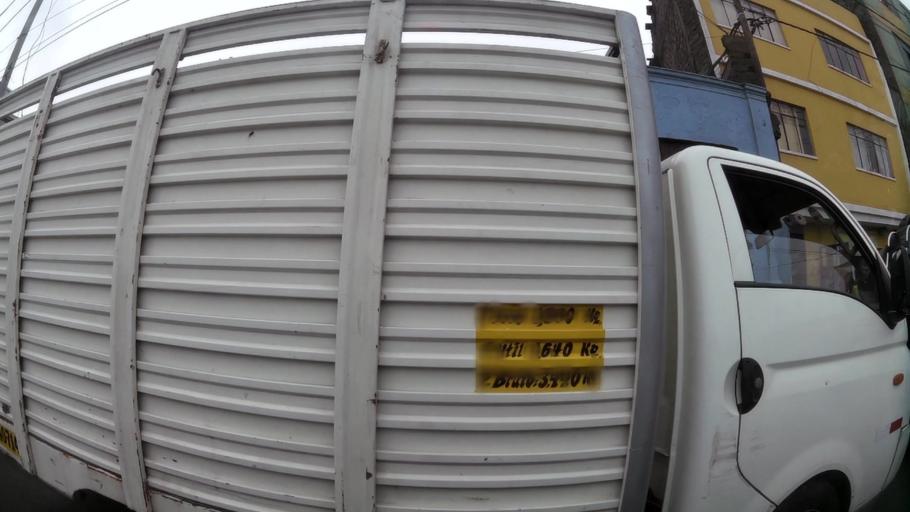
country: PE
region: Lima
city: Lima
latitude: -12.0473
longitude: -77.0184
